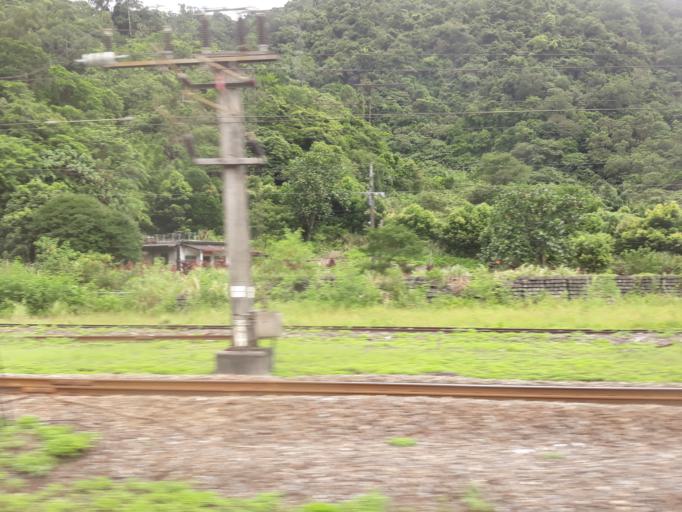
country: TW
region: Taiwan
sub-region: Yilan
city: Yilan
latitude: 24.5656
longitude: 121.8431
